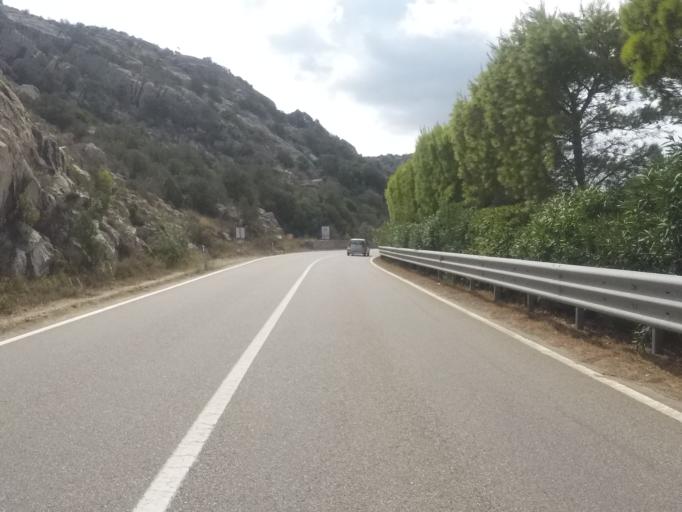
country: IT
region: Sardinia
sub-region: Provincia di Olbia-Tempio
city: Porto Cervo
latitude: 41.1363
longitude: 9.5003
